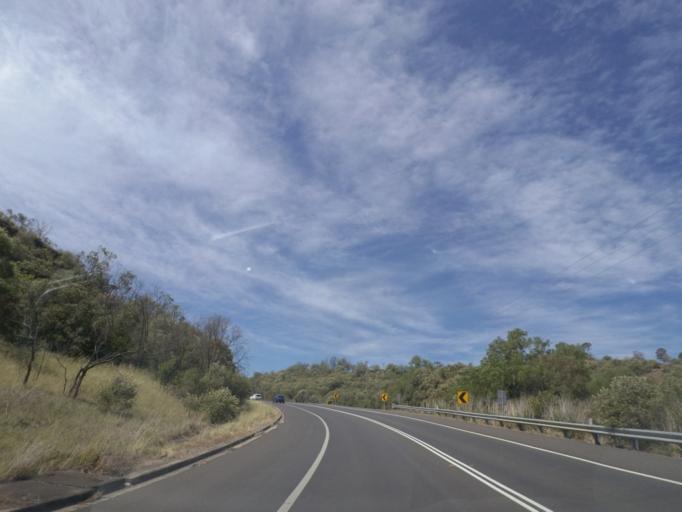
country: AU
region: New South Wales
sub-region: Wollondilly
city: Picton
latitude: -34.1571
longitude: 150.6564
